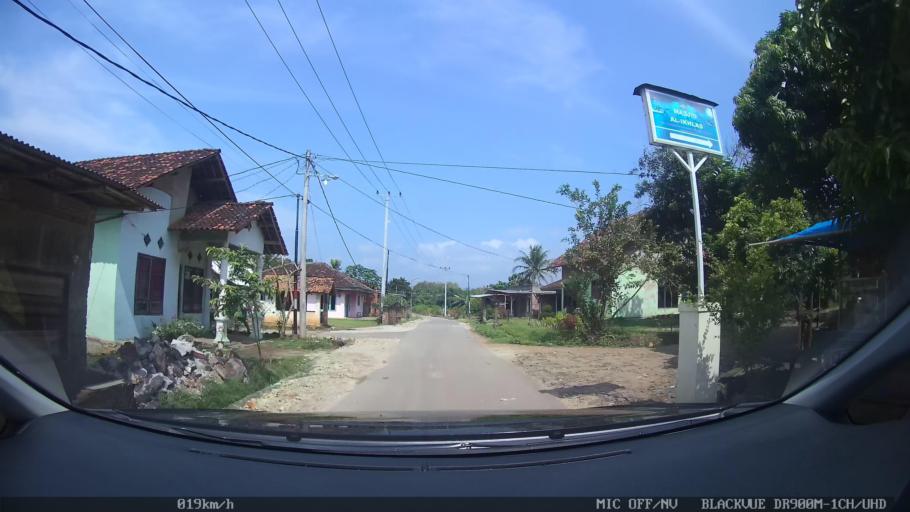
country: ID
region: Lampung
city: Kedaton
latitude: -5.3291
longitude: 105.2753
